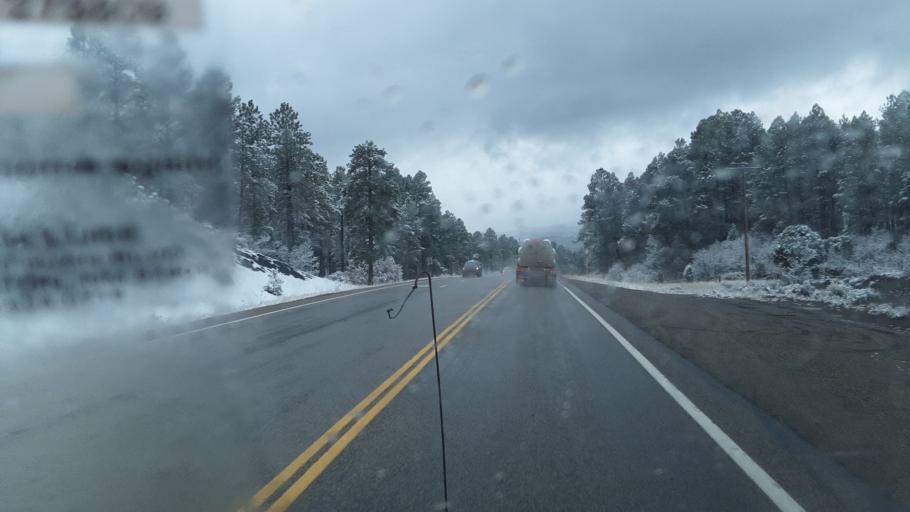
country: US
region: Colorado
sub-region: Archuleta County
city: Pagosa Springs
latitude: 37.2128
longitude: -107.2786
